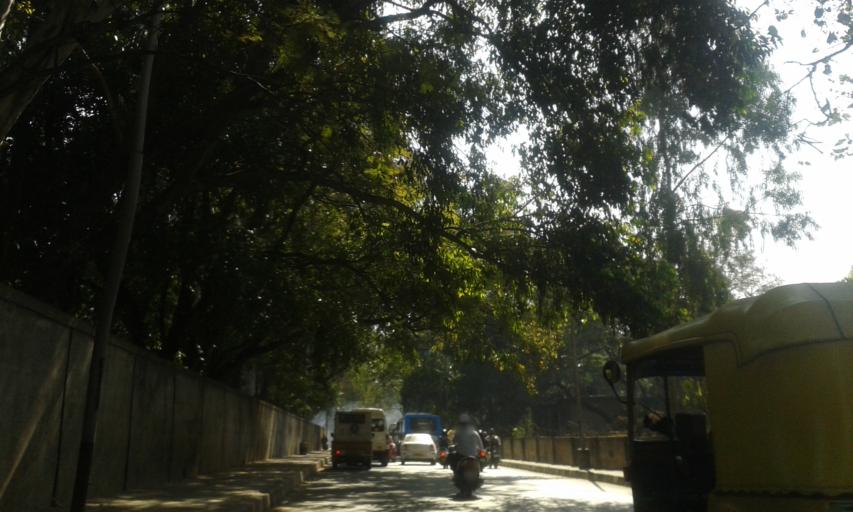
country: IN
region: Karnataka
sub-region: Bangalore Urban
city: Bangalore
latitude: 12.9681
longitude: 77.6148
